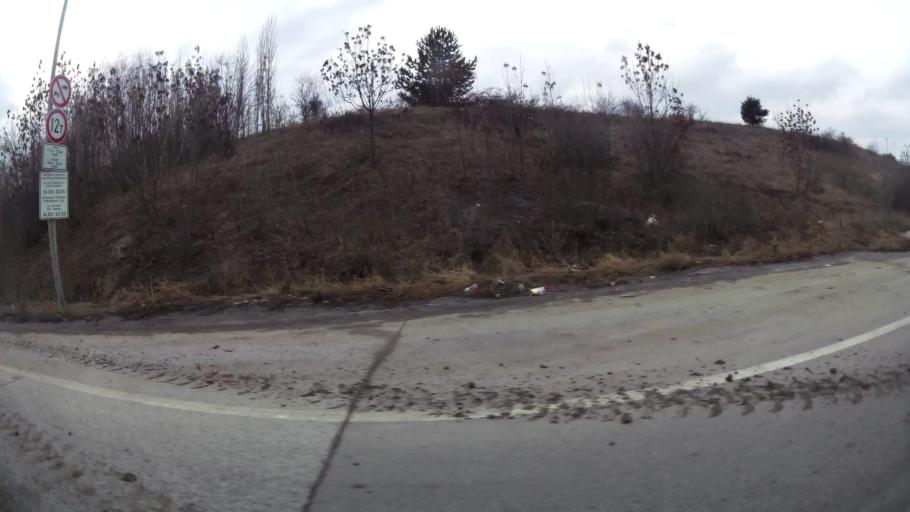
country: BG
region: Sofiya
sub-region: Obshtina Bozhurishte
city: Bozhurishte
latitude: 42.7108
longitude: 23.2303
